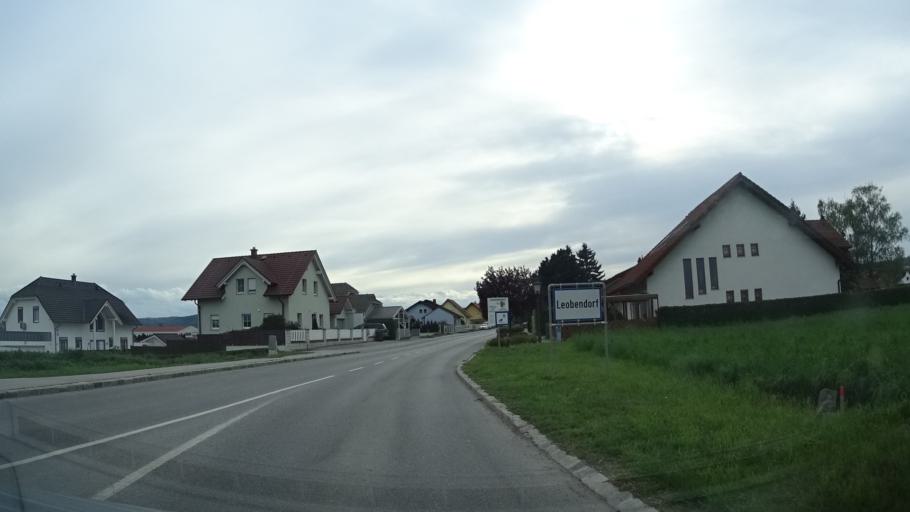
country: AT
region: Lower Austria
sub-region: Politischer Bezirk Korneuburg
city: Leobendorf
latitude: 48.3775
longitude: 16.3326
